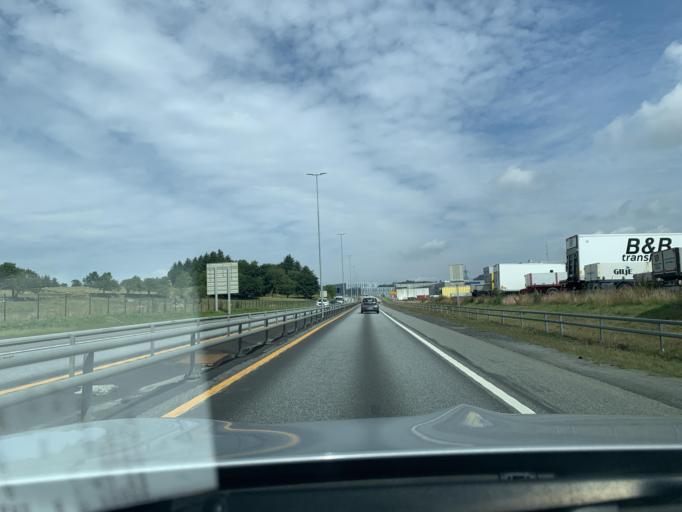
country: NO
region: Rogaland
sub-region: Sola
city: Sola
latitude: 58.9013
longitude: 5.6859
